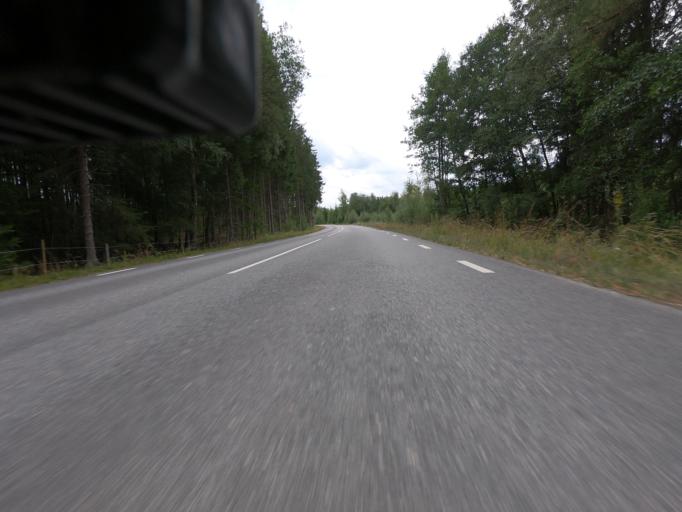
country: SE
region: Kronoberg
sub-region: Vaxjo Kommun
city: Braas
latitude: 57.1461
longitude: 14.9592
